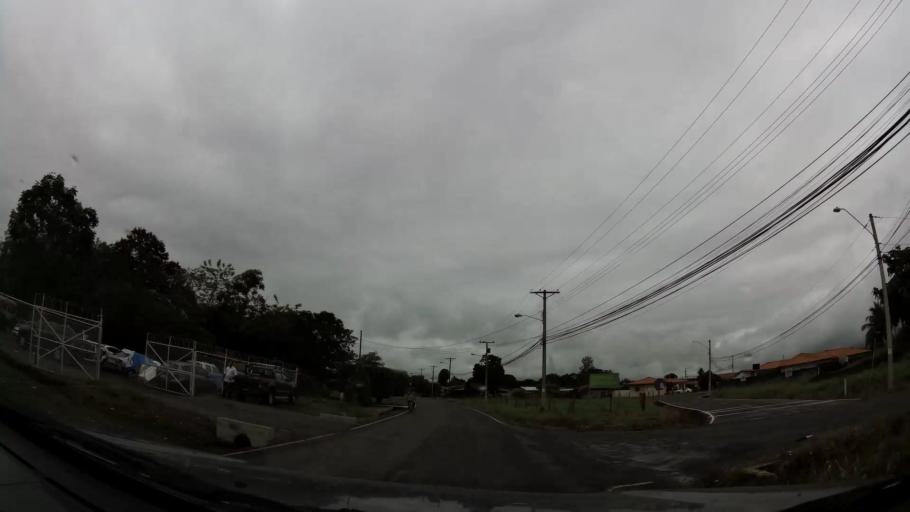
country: PA
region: Chiriqui
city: David
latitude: 8.4340
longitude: -82.4423
